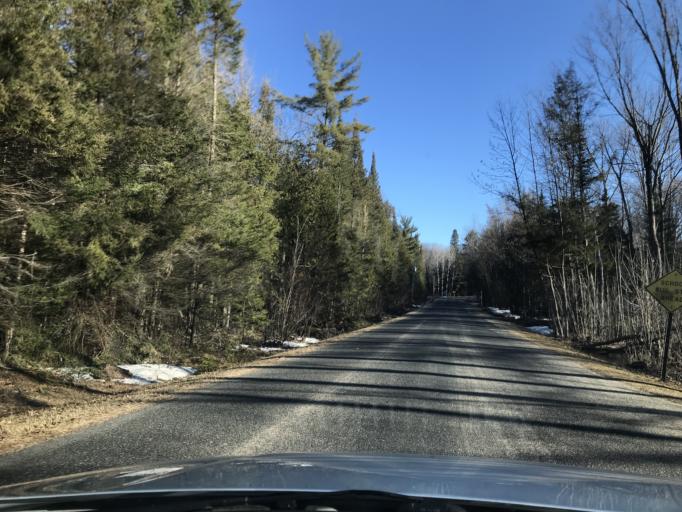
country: US
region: Wisconsin
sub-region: Marinette County
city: Niagara
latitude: 45.3661
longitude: -88.0296
